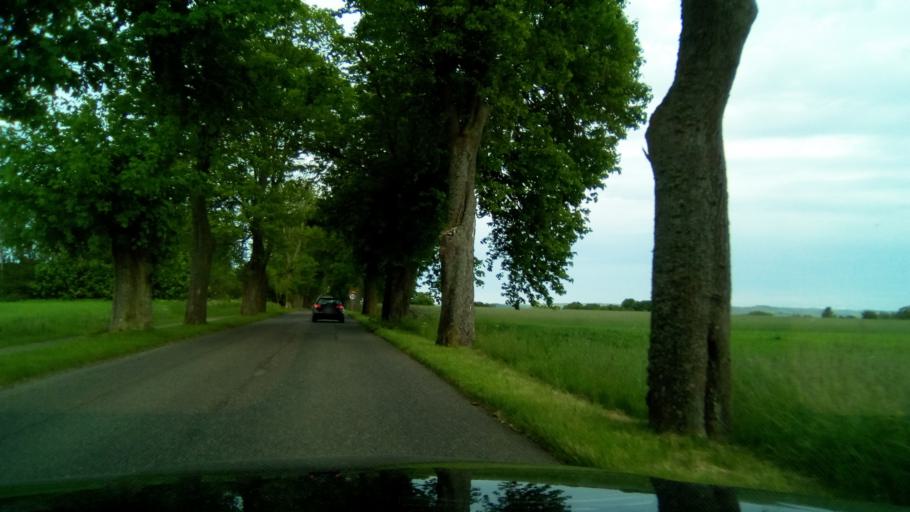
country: PL
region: Pomeranian Voivodeship
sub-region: Powiat pucki
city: Wierzchucino
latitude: 54.7905
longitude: 17.9844
